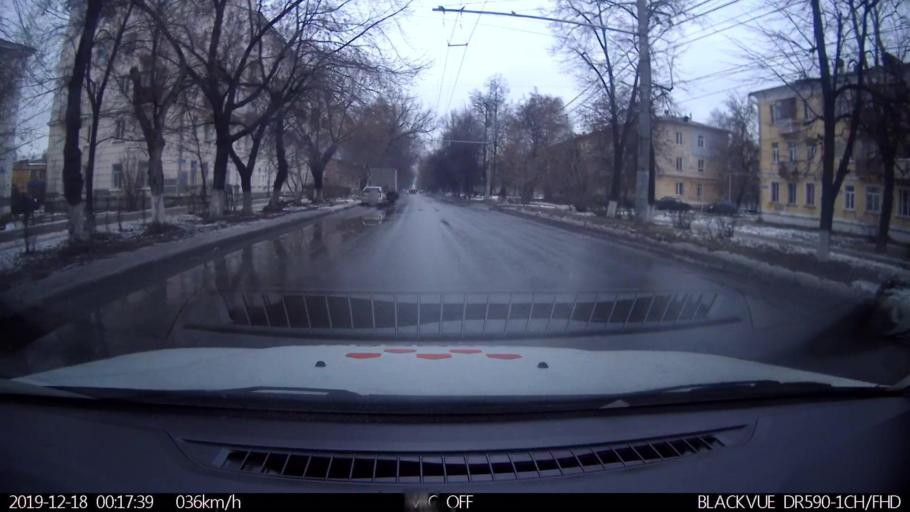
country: RU
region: Nizjnij Novgorod
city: Nizhniy Novgorod
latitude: 56.3248
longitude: 43.8817
